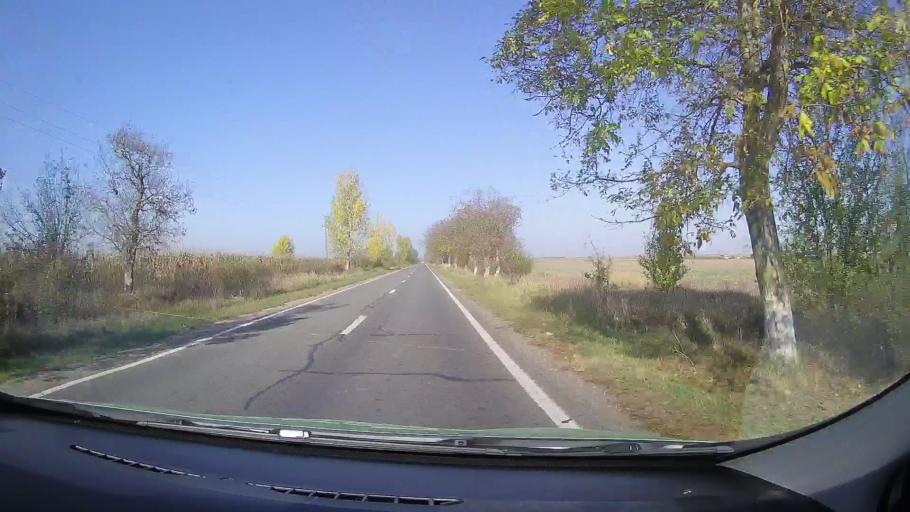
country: RO
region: Satu Mare
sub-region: Comuna Urziceni
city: Urziceni
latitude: 47.7159
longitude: 22.4216
